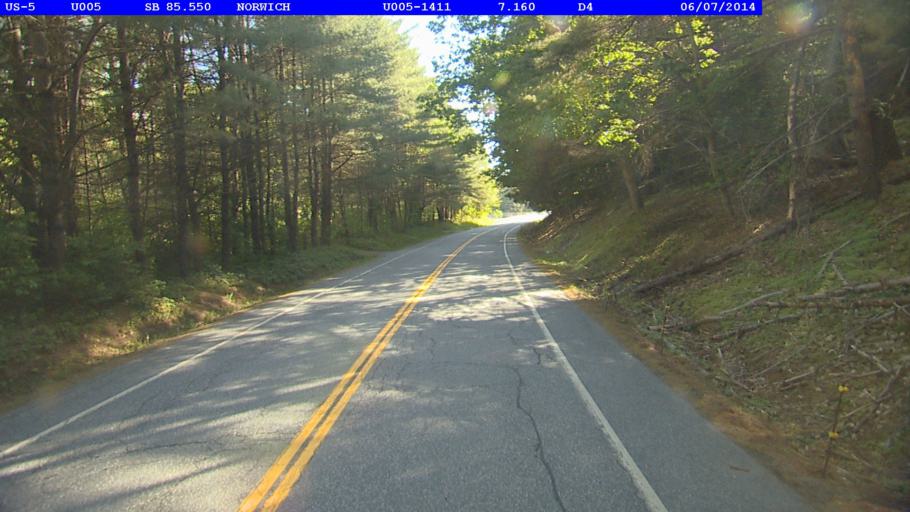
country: US
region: New Hampshire
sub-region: Grafton County
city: Lyme
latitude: 43.7613
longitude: -72.2234
